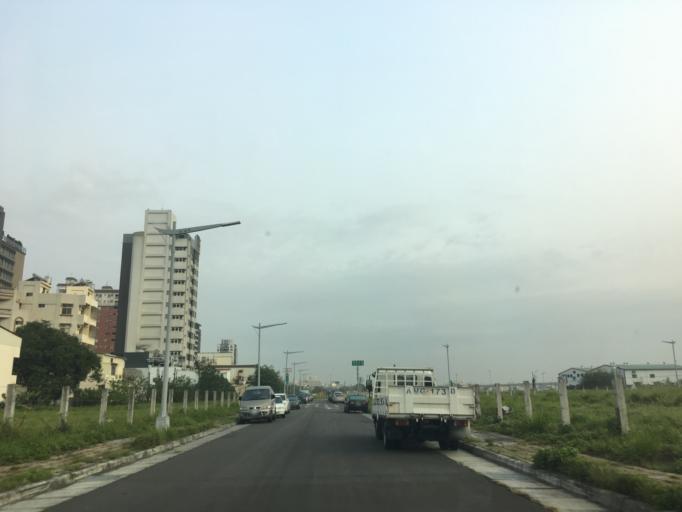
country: TW
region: Taiwan
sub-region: Taichung City
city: Taichung
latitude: 24.1902
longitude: 120.6687
